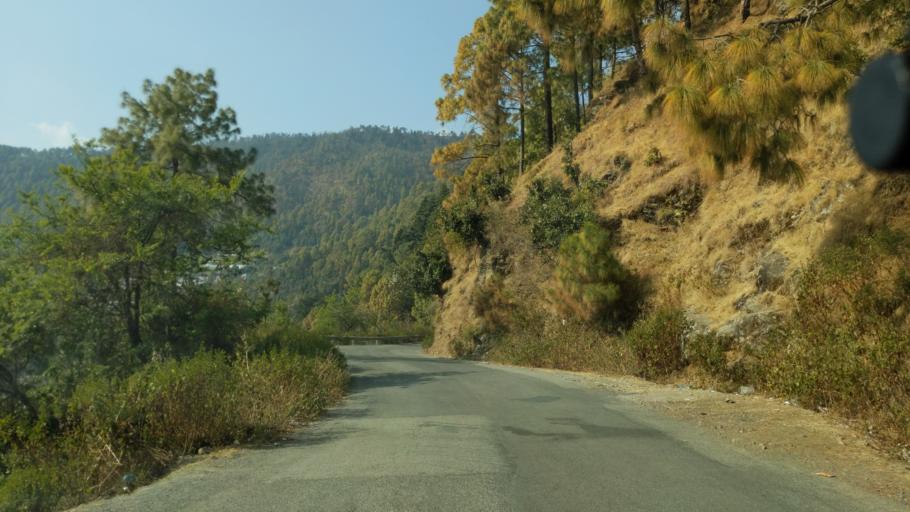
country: IN
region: Uttarakhand
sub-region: Naini Tal
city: Bhowali
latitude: 29.3900
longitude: 79.5368
